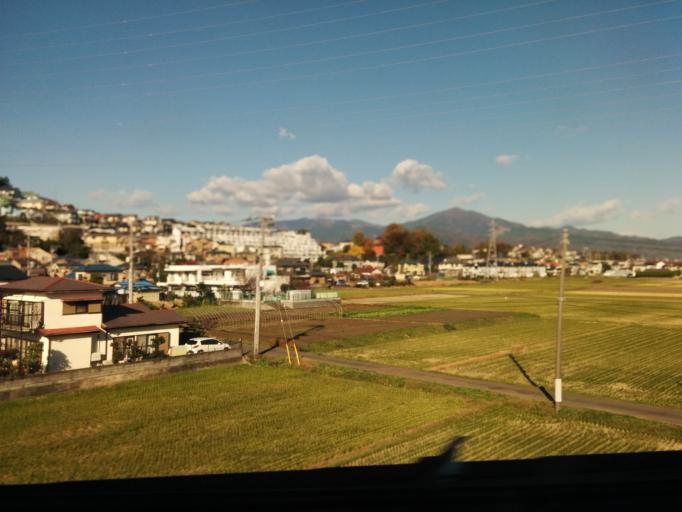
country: JP
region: Kanagawa
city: Oiso
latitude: 35.3409
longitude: 139.3061
